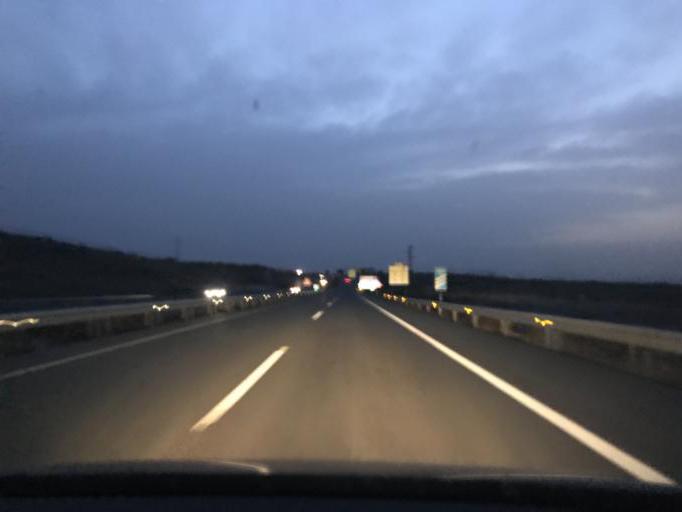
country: ES
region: Andalusia
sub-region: Provincia de Granada
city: Gor
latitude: 37.3970
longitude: -2.9807
